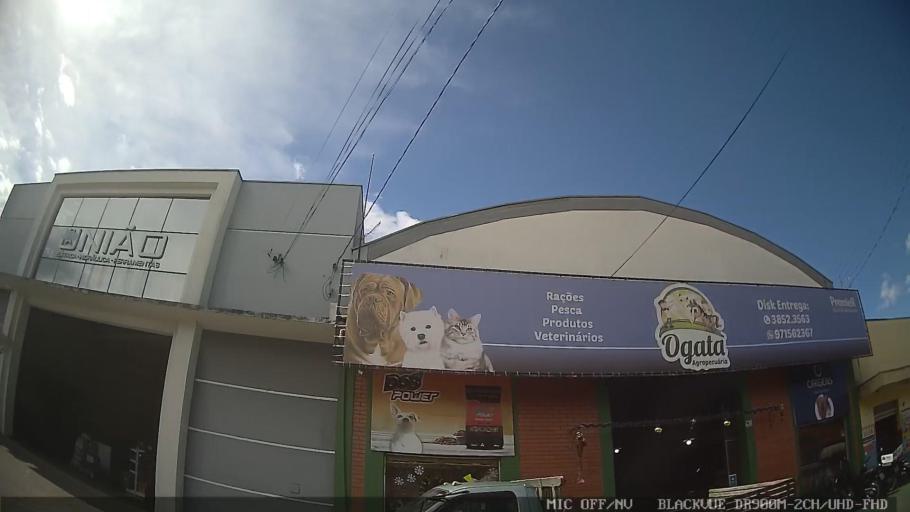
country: BR
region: Sao Paulo
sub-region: Pedreira
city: Pedreira
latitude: -22.7414
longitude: -46.8999
